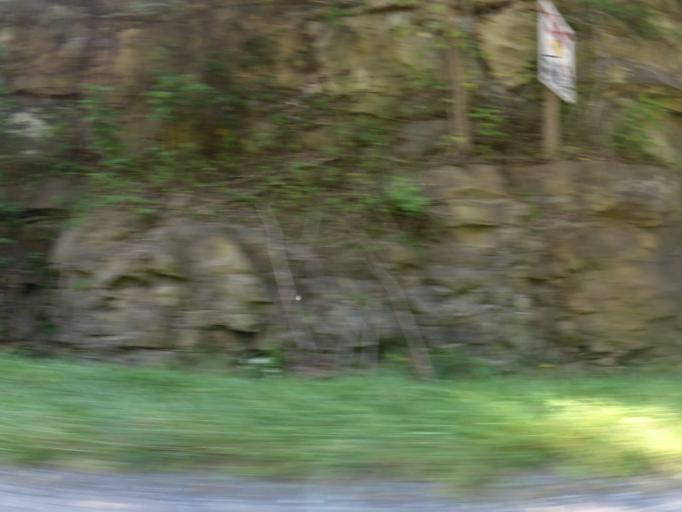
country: US
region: Kentucky
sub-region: Bell County
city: Pineville
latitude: 36.7311
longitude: -83.6139
